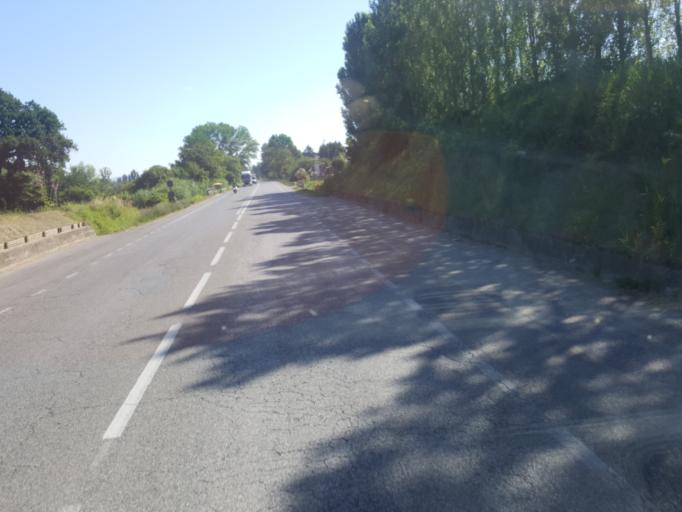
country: IT
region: The Marches
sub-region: Provincia di Pesaro e Urbino
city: Montelabbate
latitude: 43.8484
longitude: 12.7826
